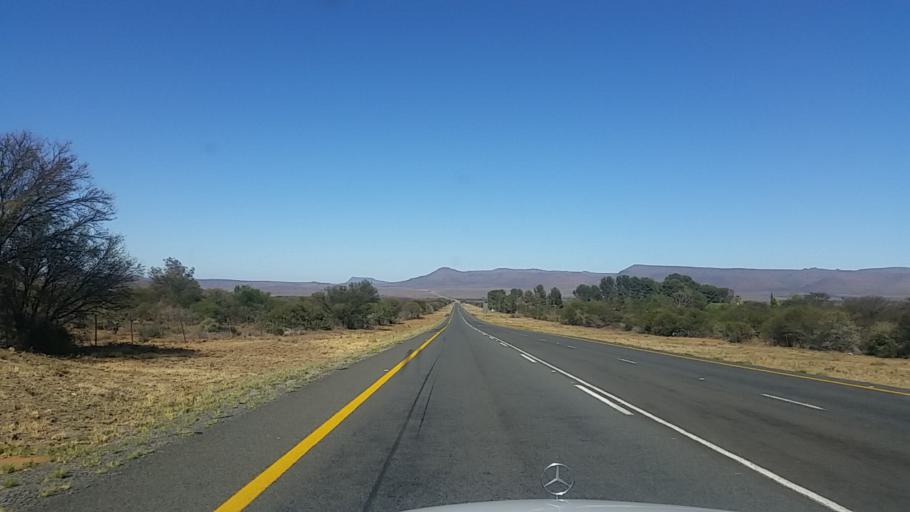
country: ZA
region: Eastern Cape
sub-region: Cacadu District Municipality
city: Graaff-Reinet
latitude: -31.9772
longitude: 24.7062
